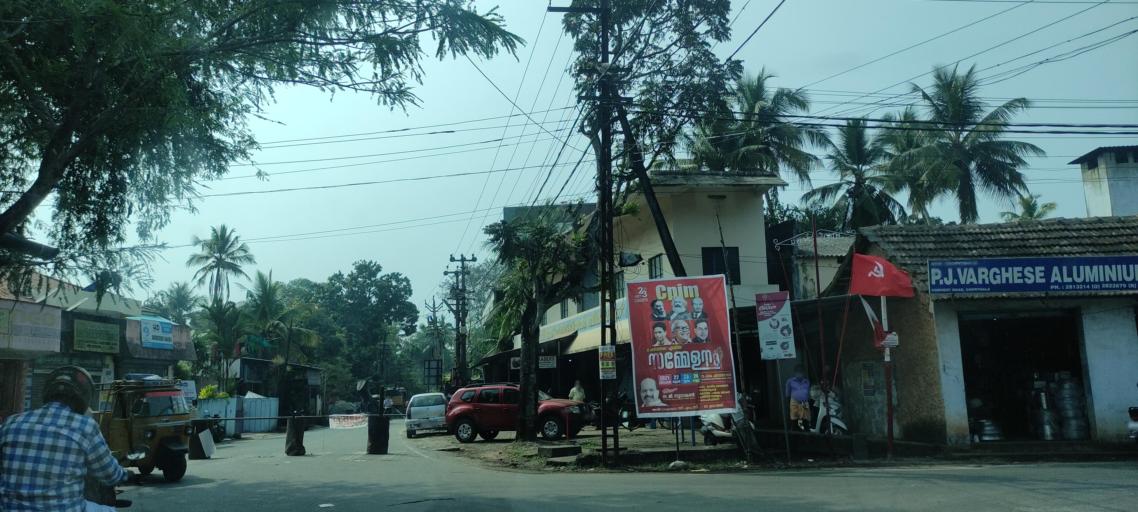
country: IN
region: Kerala
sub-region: Alappuzha
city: Vayalar
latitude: 9.6871
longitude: 76.3341
